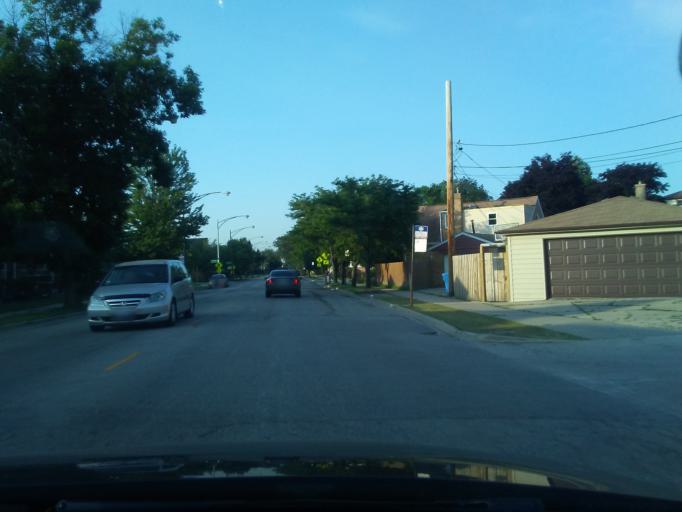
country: US
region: Illinois
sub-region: Cook County
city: Harwood Heights
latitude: 41.9909
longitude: -87.7876
